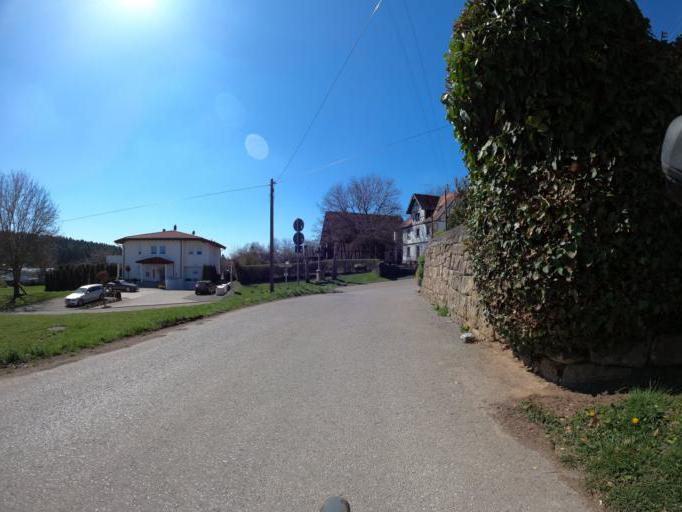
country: DE
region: Baden-Wuerttemberg
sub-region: Freiburg Region
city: Muhlheim am Bach
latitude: 48.4087
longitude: 8.6657
